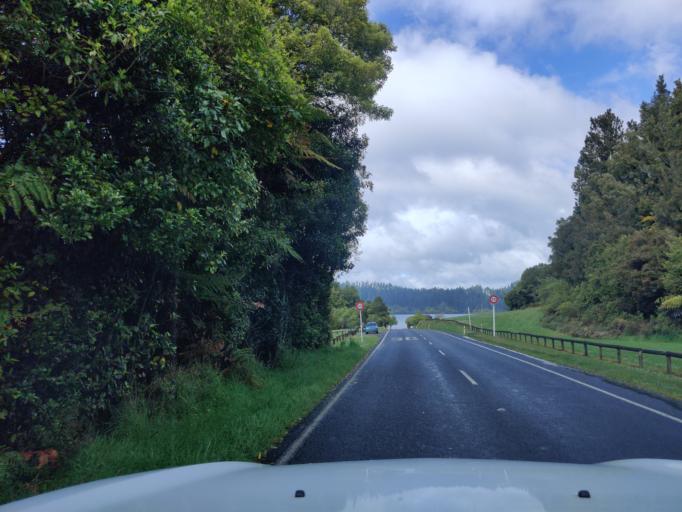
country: NZ
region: Bay of Plenty
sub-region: Rotorua District
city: Rotorua
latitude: -38.1840
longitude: 176.3282
